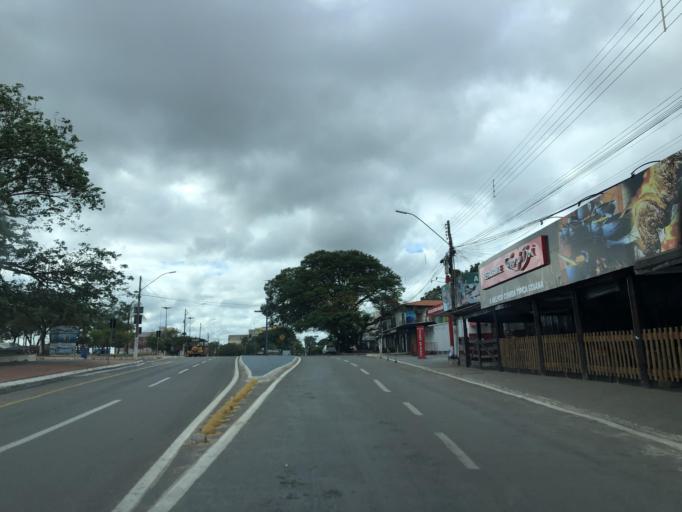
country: BR
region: Goias
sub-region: Trindade
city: Trindade
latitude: -16.6611
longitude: -49.4863
